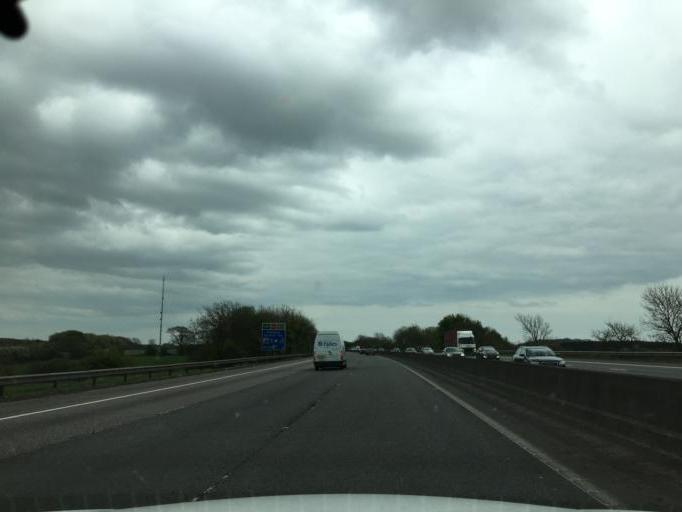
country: GB
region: England
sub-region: Wiltshire
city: Aldbourne
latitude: 51.4890
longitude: -1.5755
